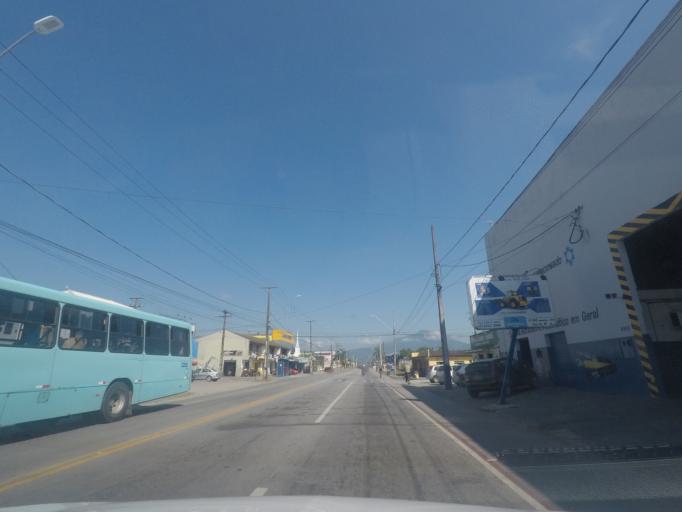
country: BR
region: Parana
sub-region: Paranagua
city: Paranagua
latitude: -25.5564
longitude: -48.5561
